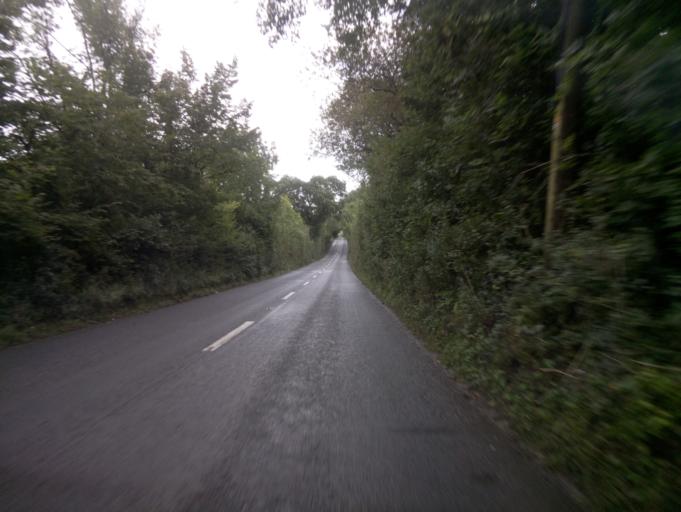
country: GB
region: England
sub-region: Devon
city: Modbury
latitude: 50.3381
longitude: -3.8574
